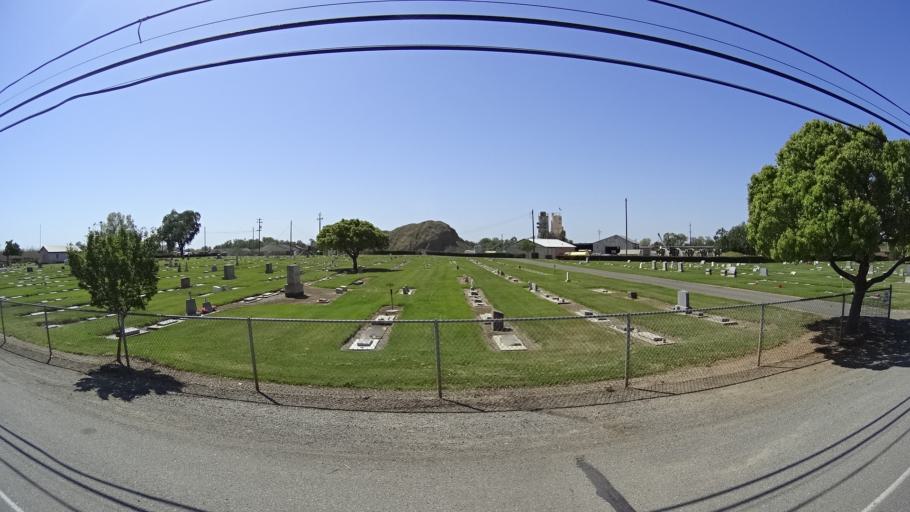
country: US
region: California
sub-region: Glenn County
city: Orland
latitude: 39.7691
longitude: -122.1953
